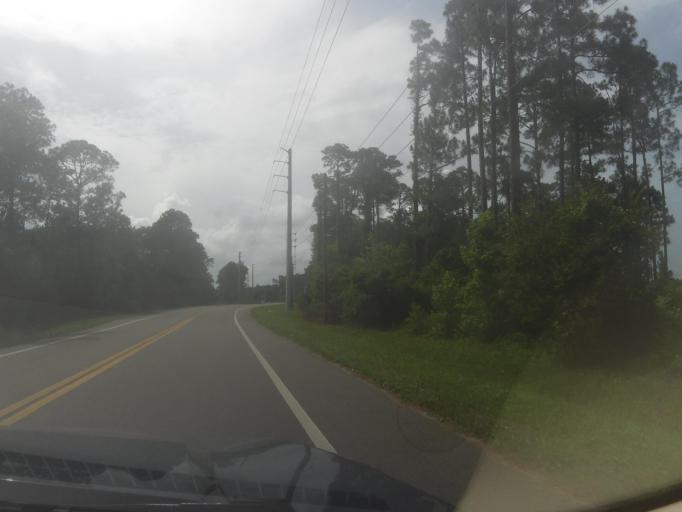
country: US
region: Florida
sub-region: Saint Johns County
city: Saint Augustine
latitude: 29.9071
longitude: -81.3569
